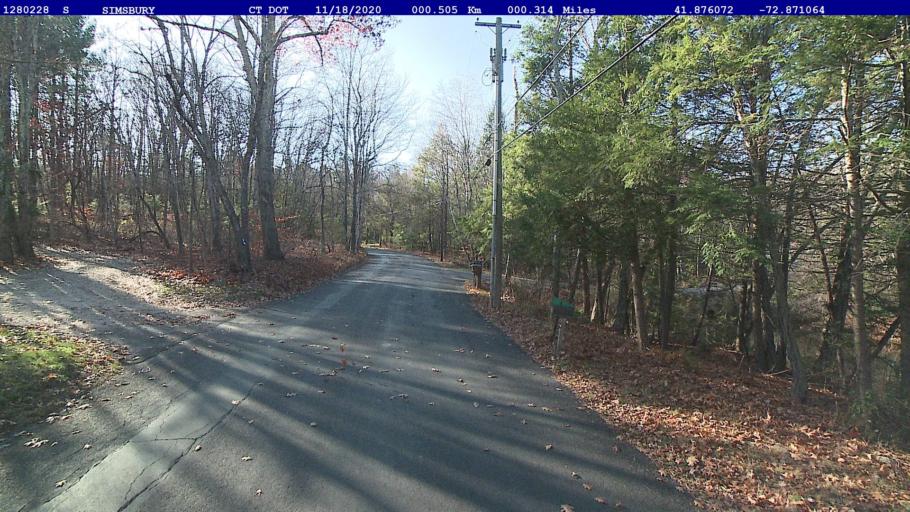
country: US
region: Connecticut
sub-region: Hartford County
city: West Simsbury
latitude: 41.8761
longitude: -72.8711
